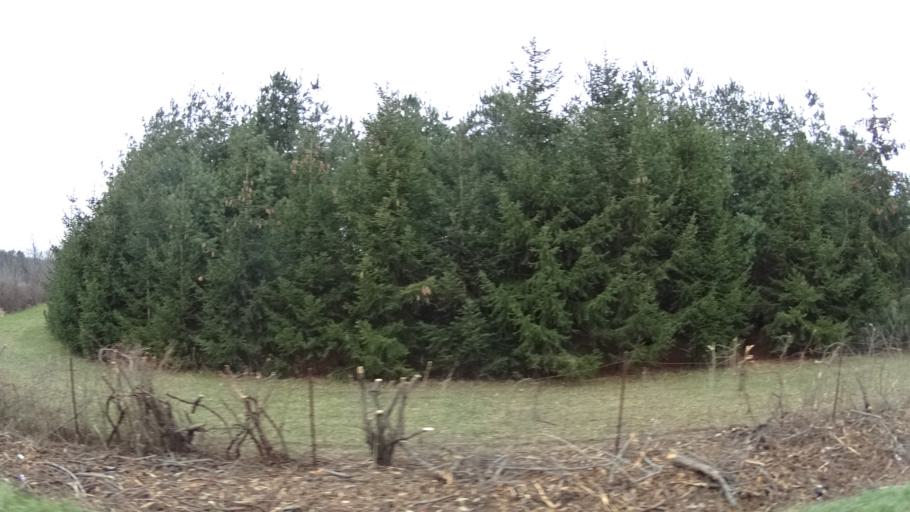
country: US
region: Ohio
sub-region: Lorain County
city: Wellington
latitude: 41.1409
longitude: -82.2692
